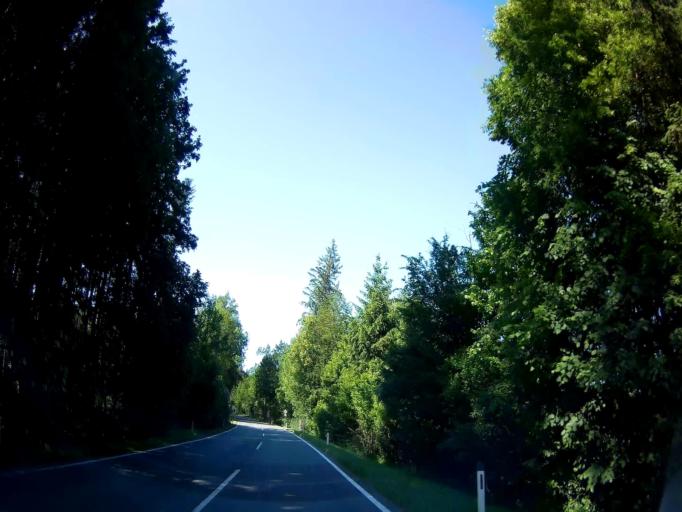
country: AT
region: Salzburg
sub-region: Politischer Bezirk Salzburg-Umgebung
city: Dorfbeuern
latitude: 48.0231
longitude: 12.9719
